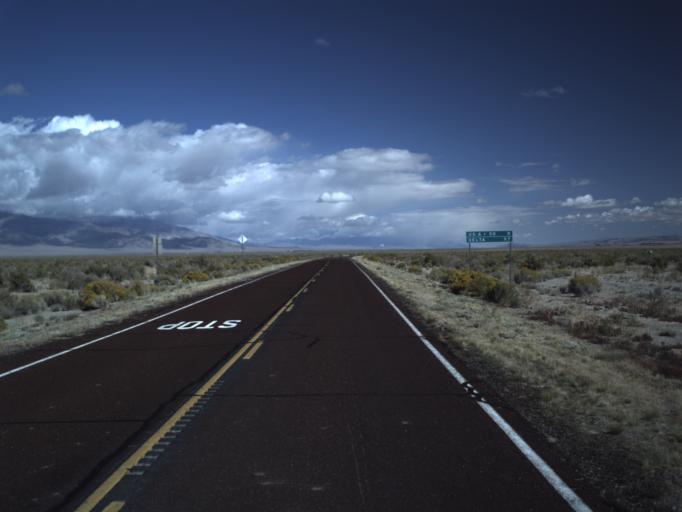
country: US
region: Nevada
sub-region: White Pine County
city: McGill
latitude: 38.9413
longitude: -114.0334
